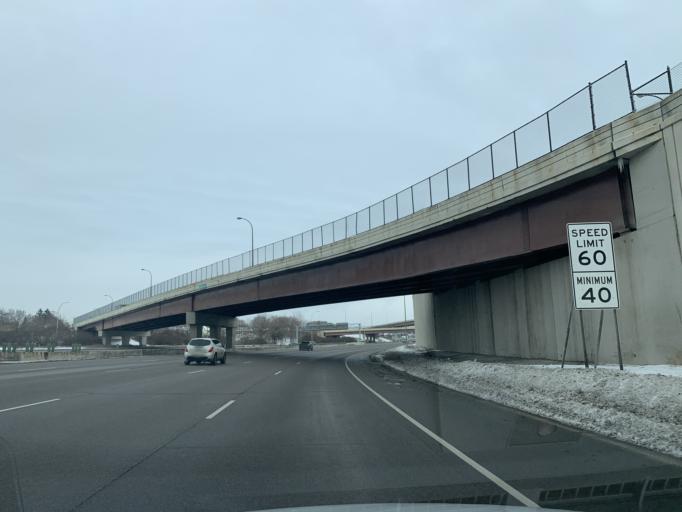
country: US
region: Minnesota
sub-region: Hennepin County
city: Minneapolis
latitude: 44.9892
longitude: -93.2880
